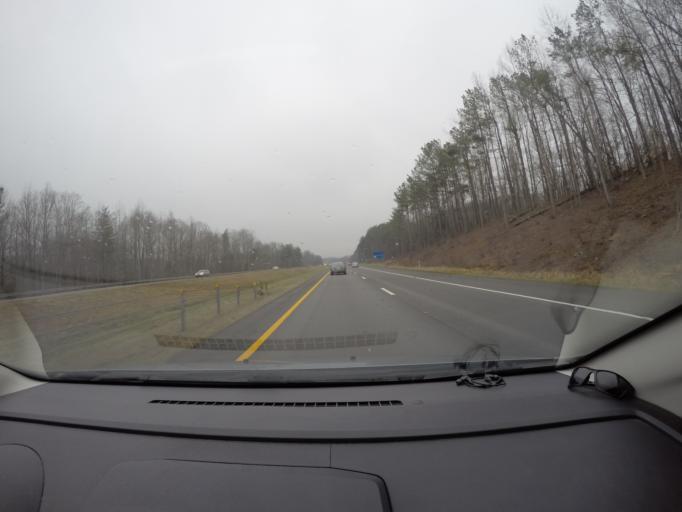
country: US
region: Tennessee
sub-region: Coffee County
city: New Union
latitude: 35.5461
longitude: -86.1852
